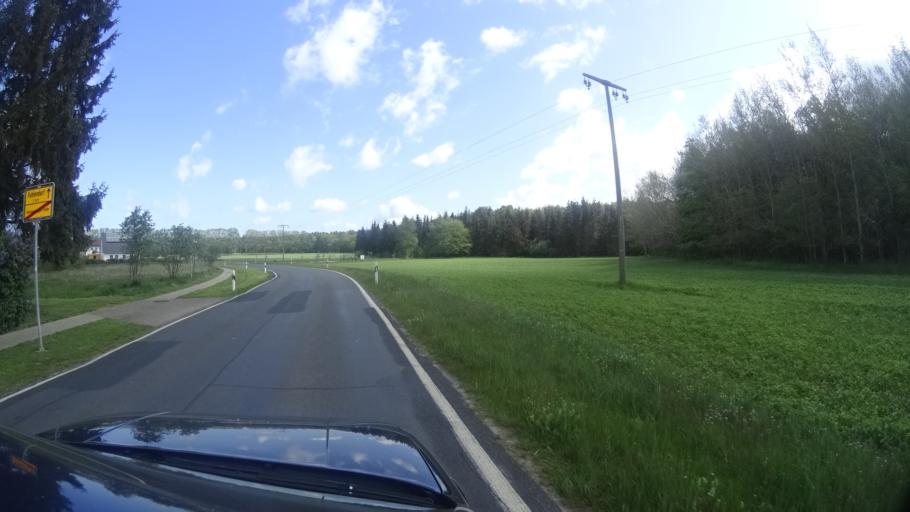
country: DE
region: Mecklenburg-Vorpommern
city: Born
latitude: 54.3401
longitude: 12.5897
